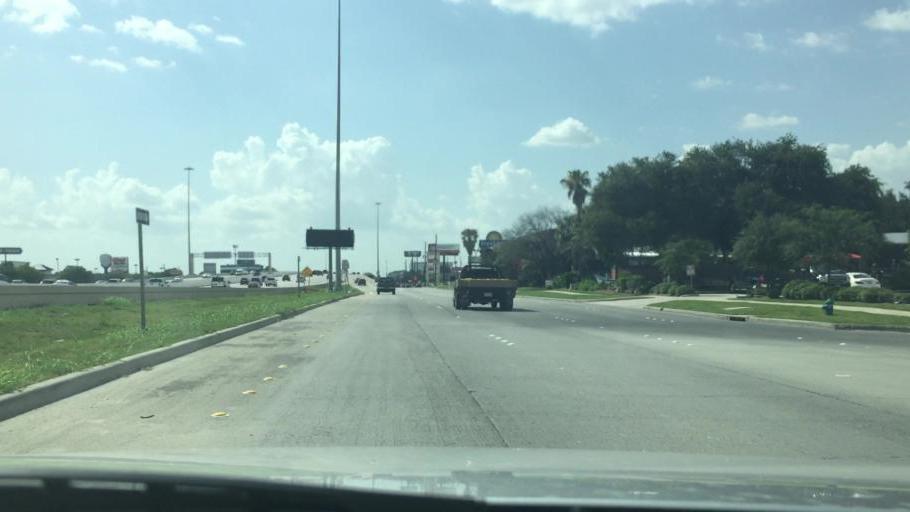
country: US
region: Texas
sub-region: Harris County
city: Spring Valley
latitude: 29.8181
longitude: -95.4642
